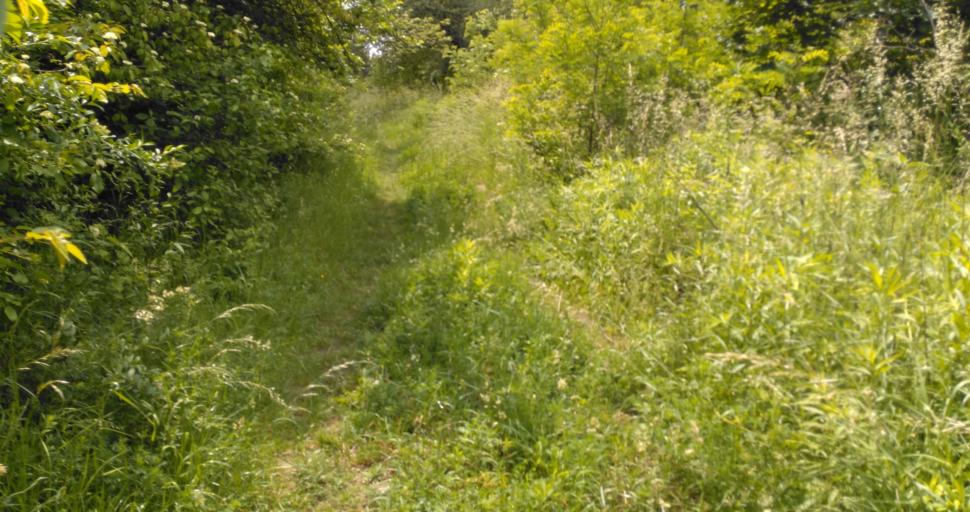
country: CZ
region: South Moravian
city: Podoli
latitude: 49.1905
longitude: 16.6721
